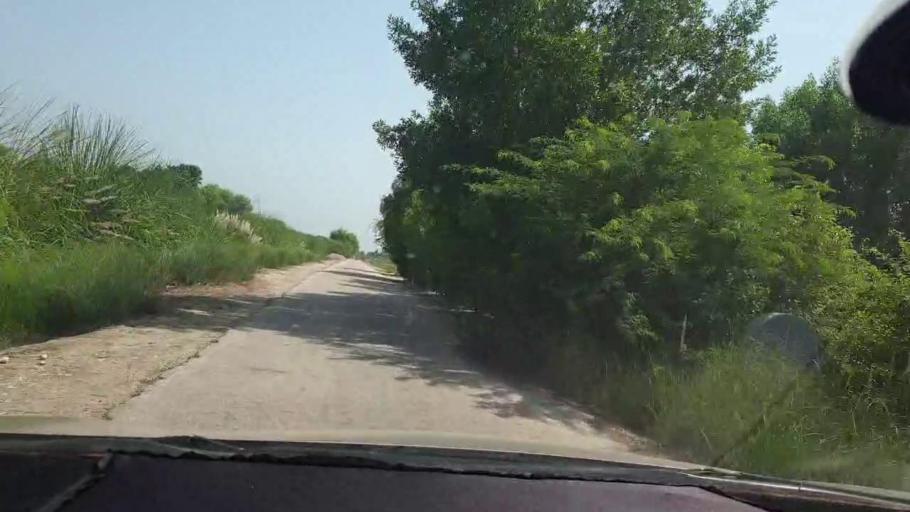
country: PK
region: Sindh
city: Kambar
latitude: 27.5202
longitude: 68.0088
